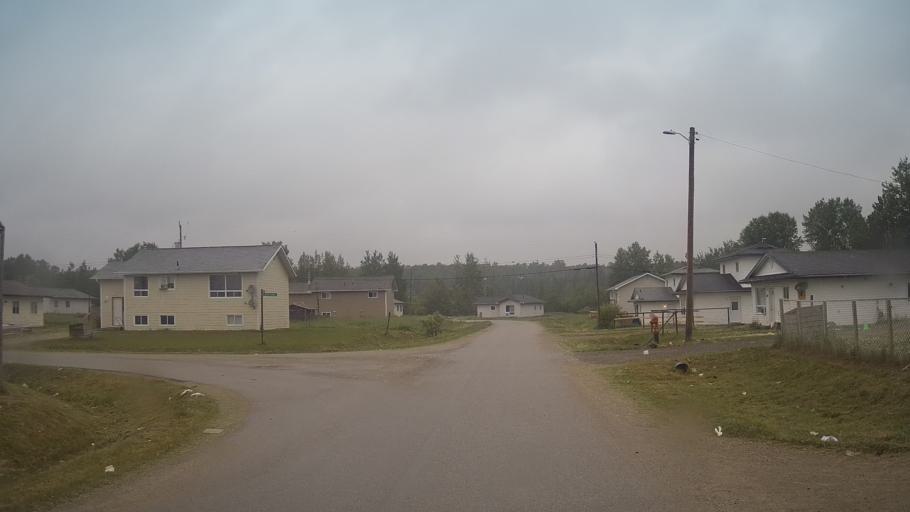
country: CA
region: Ontario
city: Greenstone
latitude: 49.7874
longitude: -86.5687
